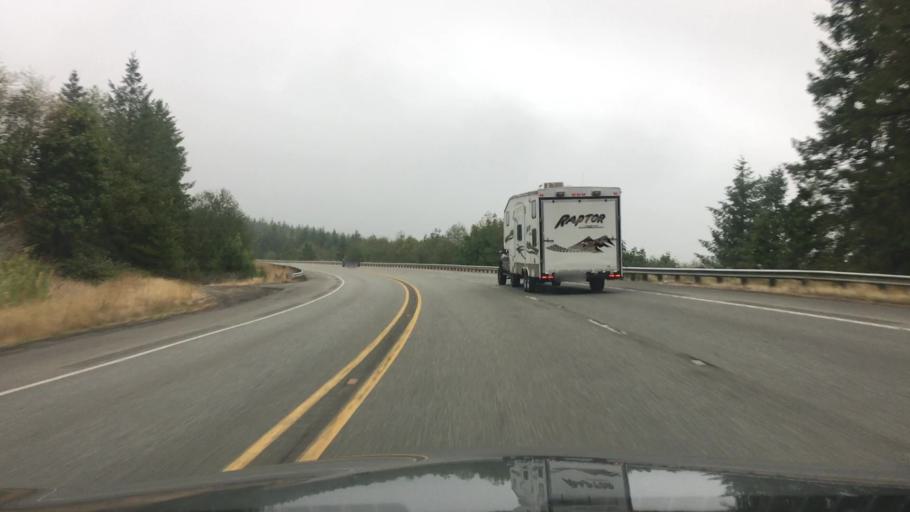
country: US
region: Washington
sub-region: Jefferson County
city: Port Hadlock-Irondale
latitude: 47.9448
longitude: -122.8822
